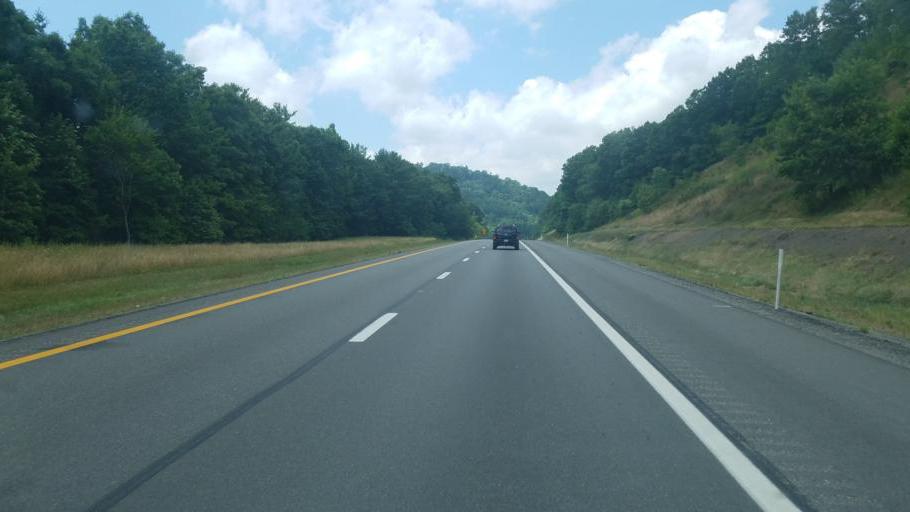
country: US
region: West Virginia
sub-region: Raleigh County
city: Beaver
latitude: 37.7054
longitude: -81.1454
